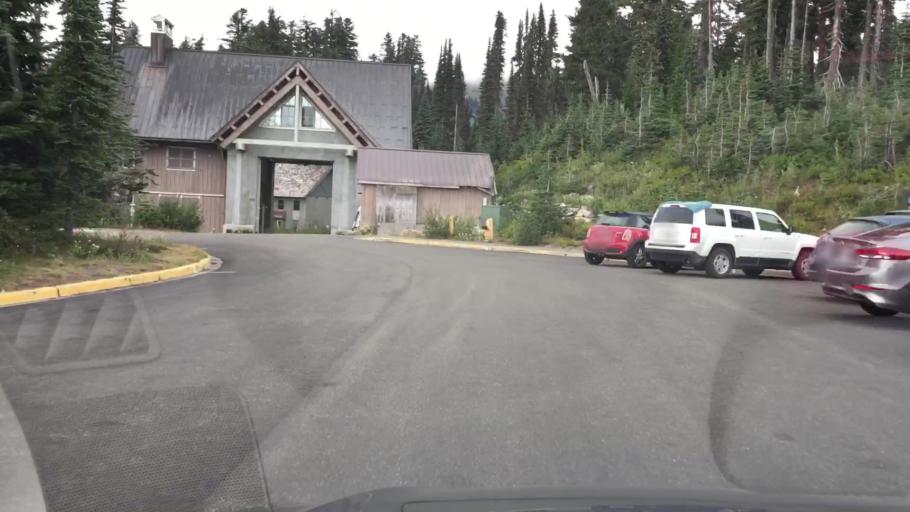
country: US
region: Washington
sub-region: Pierce County
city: Buckley
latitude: 46.7848
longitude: -121.7416
